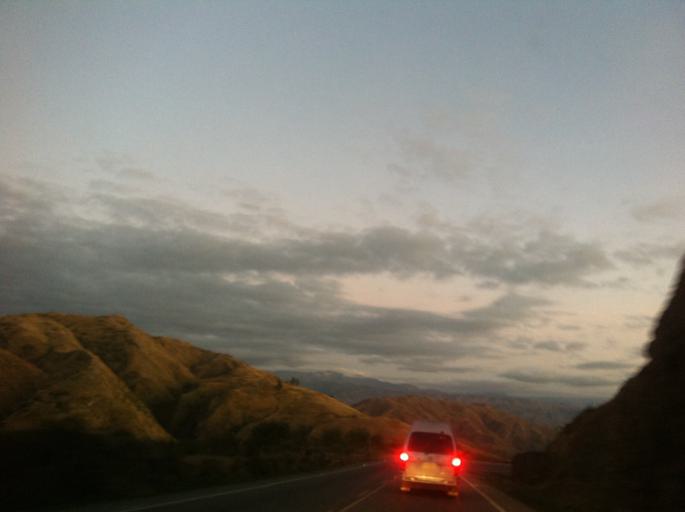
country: BO
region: Cochabamba
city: Irpa Irpa
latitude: -17.6617
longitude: -66.4279
